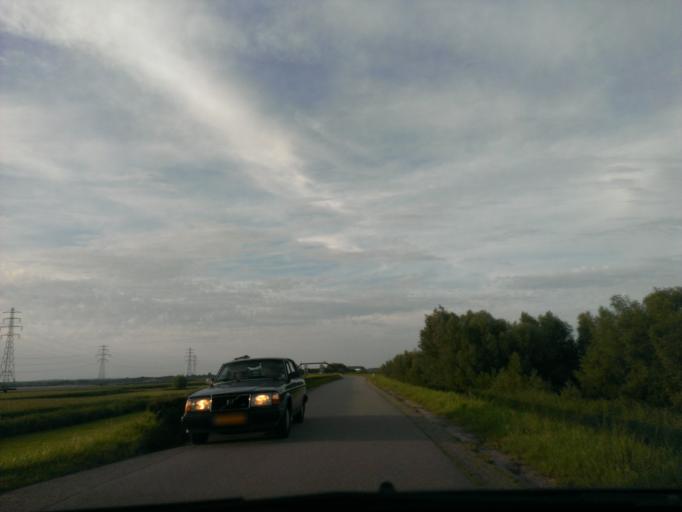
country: NL
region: Gelderland
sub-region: Gemeente Epe
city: Oene
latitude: 52.3682
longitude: 6.0741
